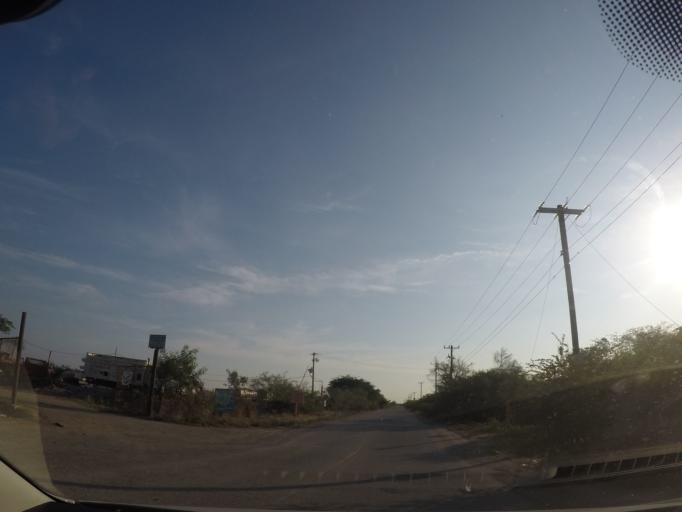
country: MX
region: Oaxaca
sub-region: Salina Cruz
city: Salina Cruz
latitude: 16.2234
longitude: -95.1882
